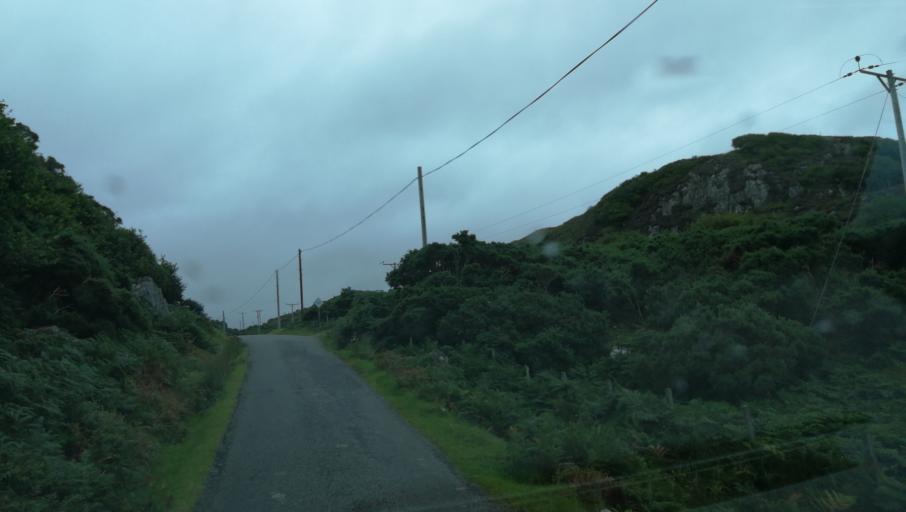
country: GB
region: Scotland
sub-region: Highland
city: Ullapool
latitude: 58.1276
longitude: -5.2635
